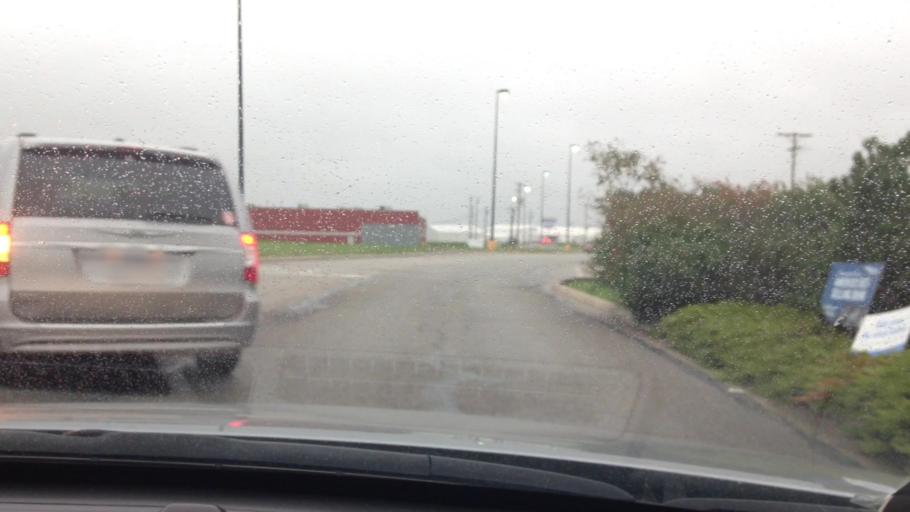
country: US
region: Kansas
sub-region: Brown County
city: Hiawatha
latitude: 39.8465
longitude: -95.5618
